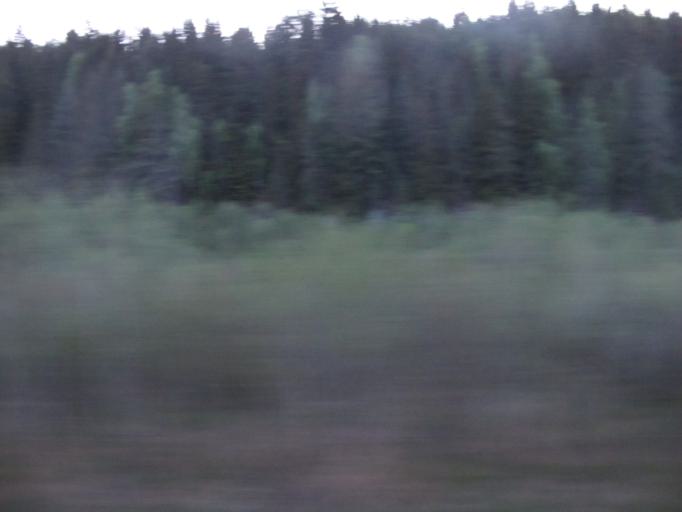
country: NO
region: Oppland
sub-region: Ringebu
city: Ringebu
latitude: 61.5343
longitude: 10.1102
